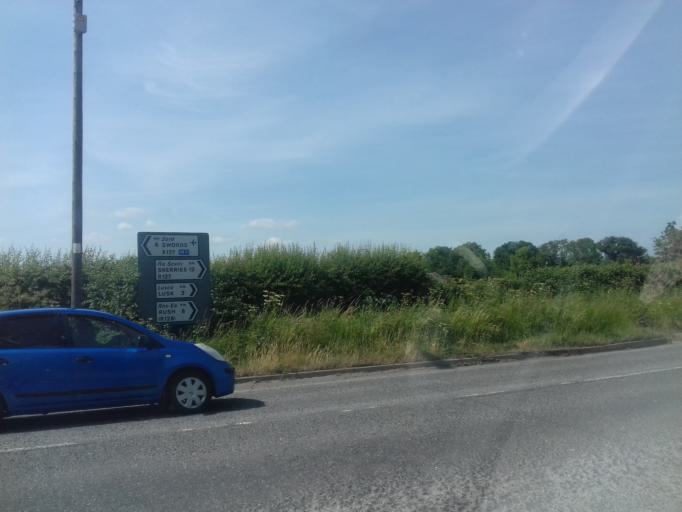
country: IE
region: Leinster
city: Lusk
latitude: 53.5050
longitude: -6.1868
